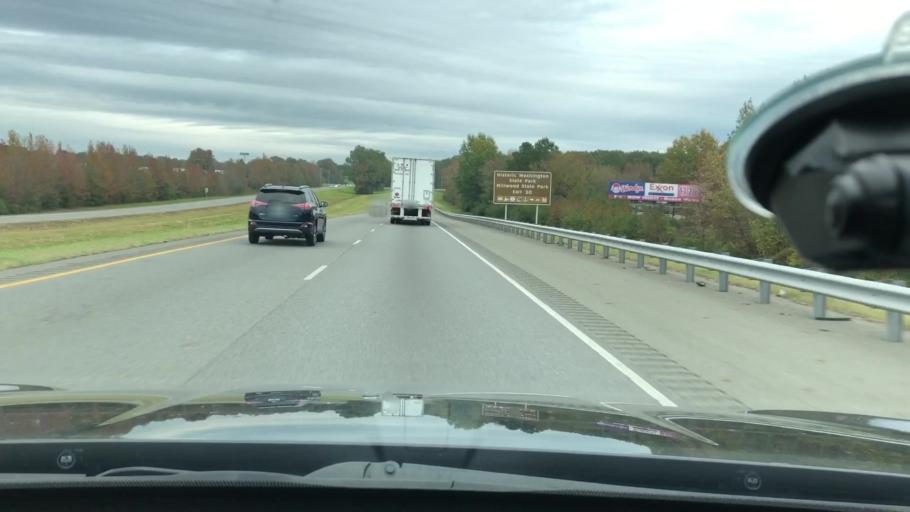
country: US
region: Arkansas
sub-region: Hempstead County
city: Hope
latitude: 33.6758
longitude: -93.6187
